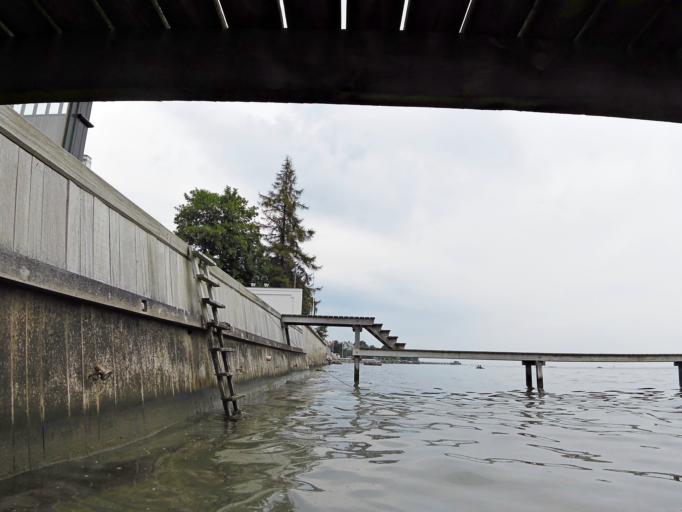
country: DK
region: Capital Region
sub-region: Gentofte Kommune
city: Charlottenlund
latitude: 55.7374
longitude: 12.5833
